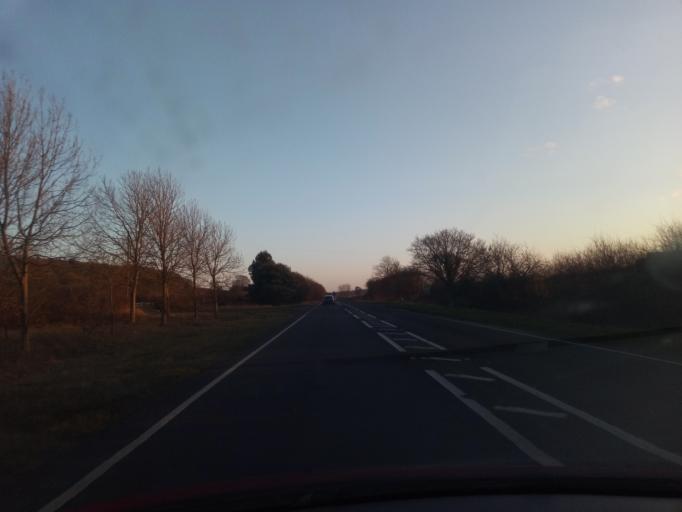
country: GB
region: England
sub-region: Nottinghamshire
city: Farnsfield
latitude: 53.0485
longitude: -1.0645
